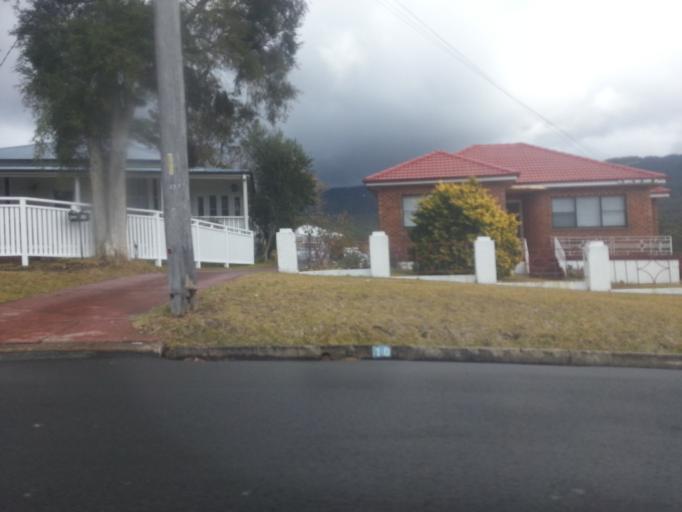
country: AU
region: New South Wales
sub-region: Wollongong
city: Bulli
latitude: -34.3251
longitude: 150.9140
